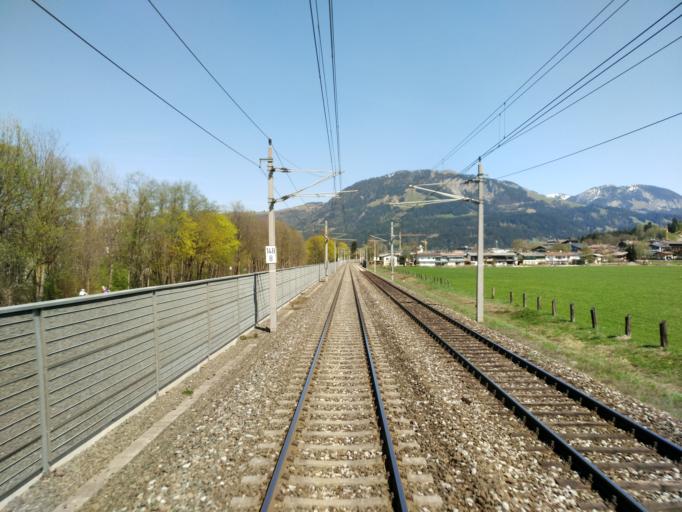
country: AT
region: Tyrol
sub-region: Politischer Bezirk Kitzbuhel
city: Sankt Johann in Tirol
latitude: 47.5181
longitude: 12.4159
